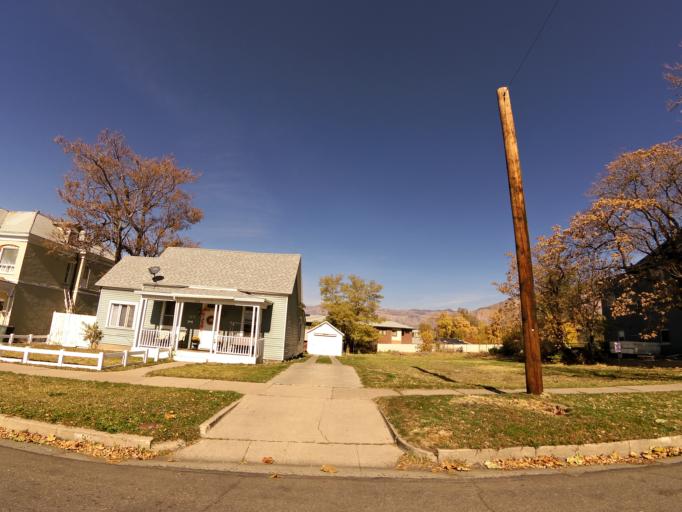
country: US
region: Utah
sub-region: Weber County
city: Ogden
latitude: 41.2249
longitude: -111.9669
